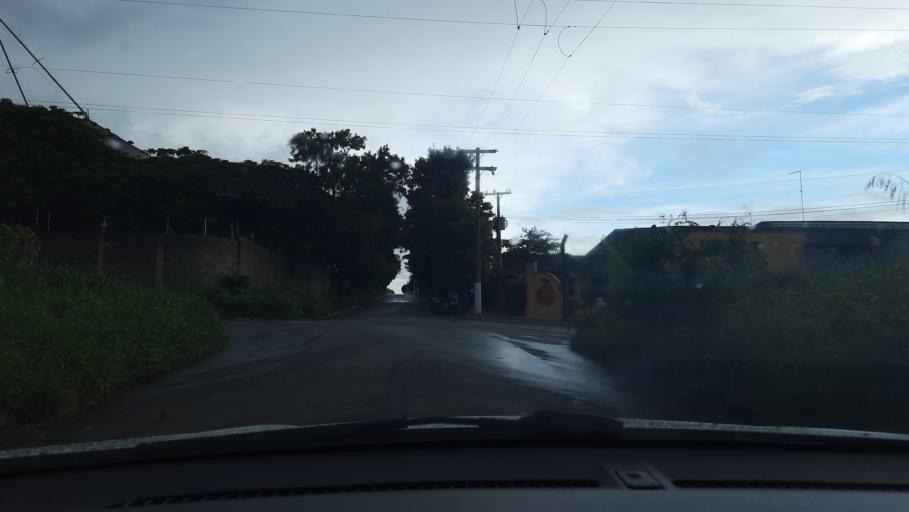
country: BR
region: Sao Paulo
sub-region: Casa Branca
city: Casa Branca
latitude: -21.7521
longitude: -47.0728
